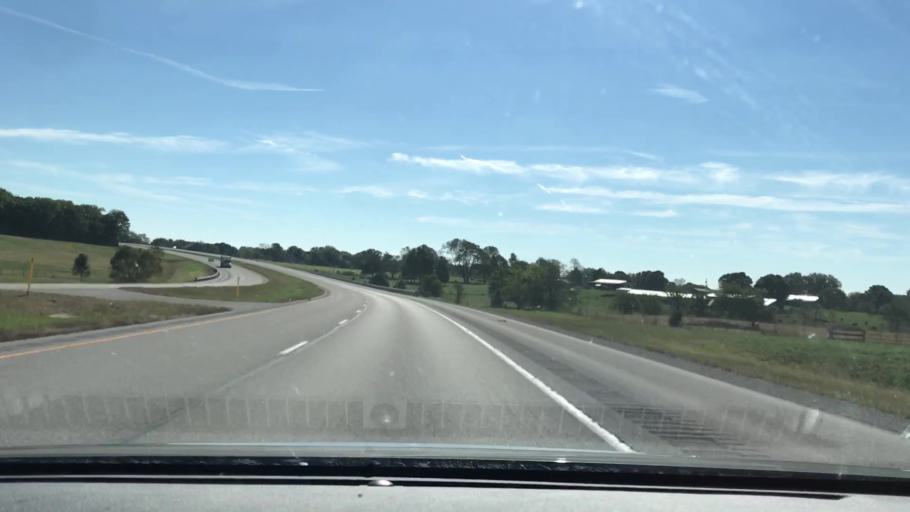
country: US
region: Kentucky
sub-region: Todd County
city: Elkton
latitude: 36.8118
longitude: -87.1378
